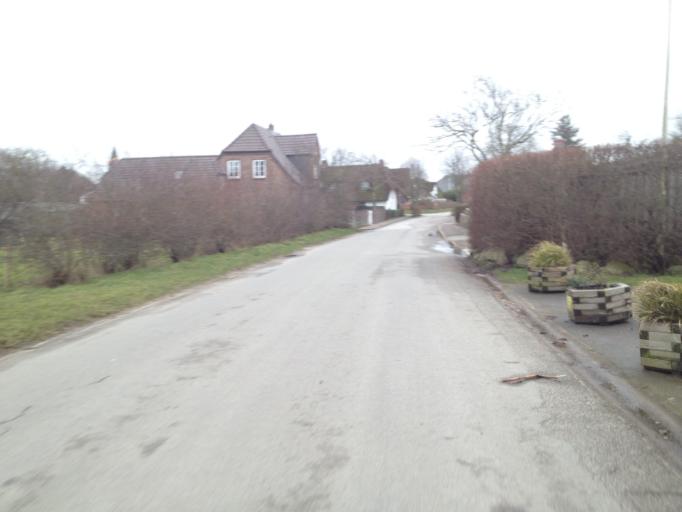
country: DE
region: Schleswig-Holstein
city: Nebel
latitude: 54.6548
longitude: 8.3530
